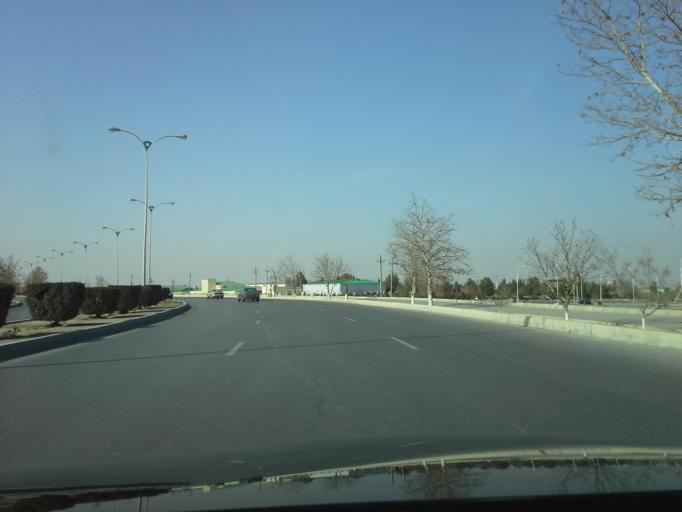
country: TM
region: Ahal
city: Abadan
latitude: 38.0552
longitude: 58.1823
